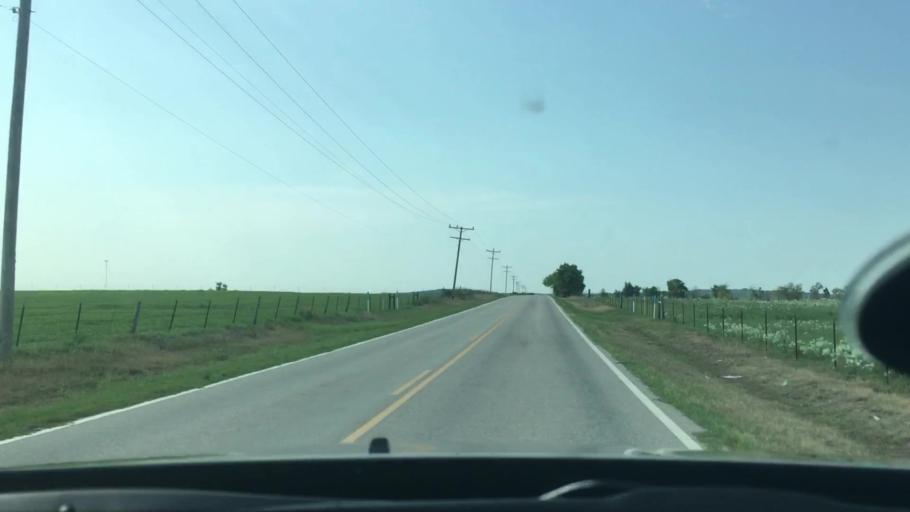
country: US
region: Oklahoma
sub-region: Bryan County
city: Durant
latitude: 34.1118
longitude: -96.4877
